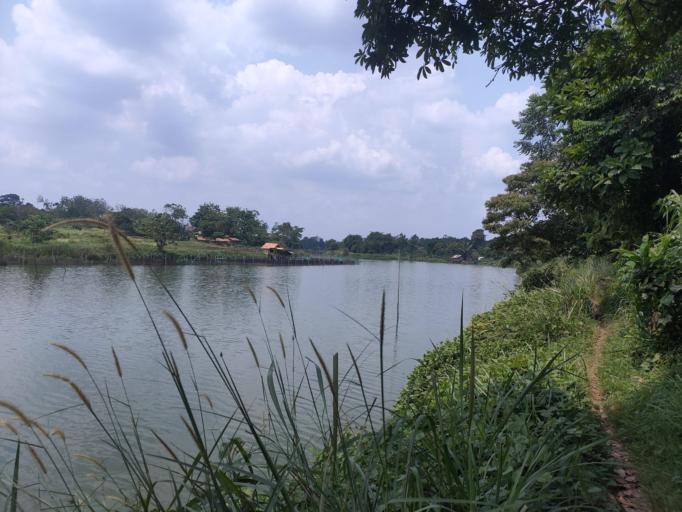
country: ID
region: West Java
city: Parung
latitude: -6.4721
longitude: 106.7152
